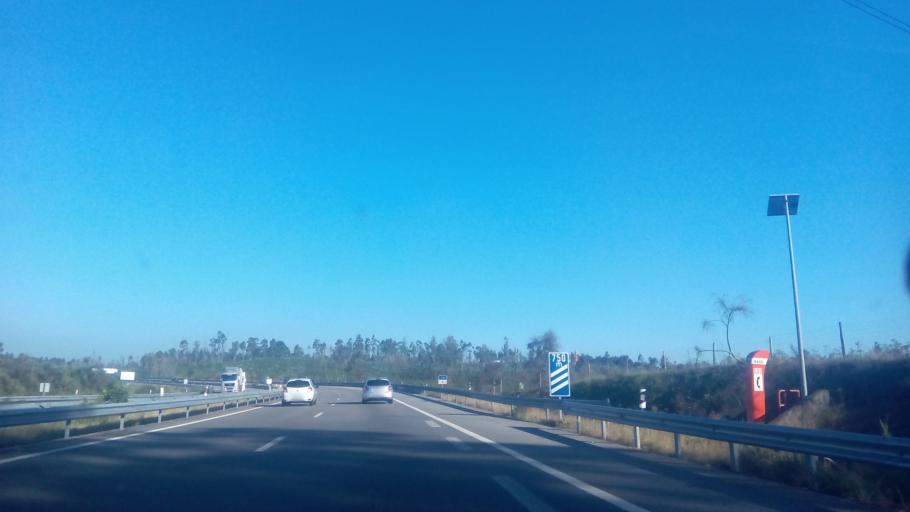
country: PT
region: Porto
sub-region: Pacos de Ferreira
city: Pacos de Ferreira
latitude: 41.2621
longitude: -8.3746
